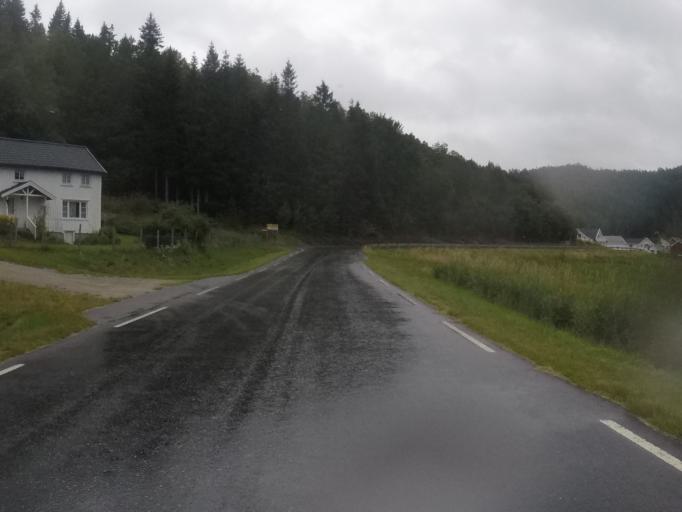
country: NO
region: Vest-Agder
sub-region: Audnedal
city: Konsmo
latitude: 58.2788
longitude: 7.2865
